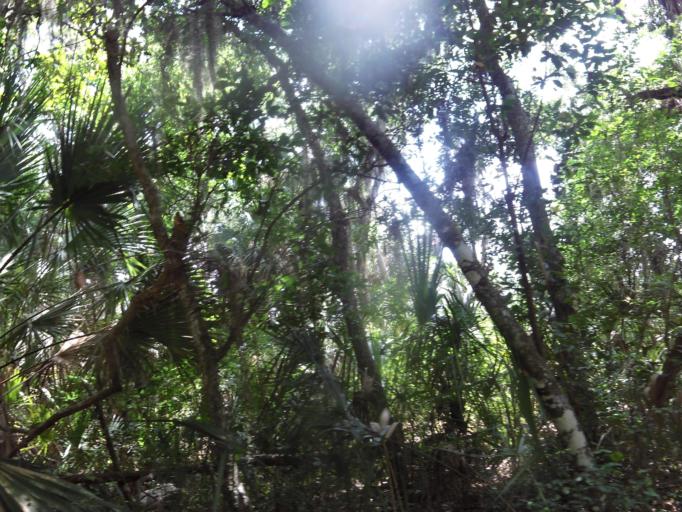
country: US
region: Florida
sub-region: Flagler County
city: Palm Coast
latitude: 29.6251
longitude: -81.2074
